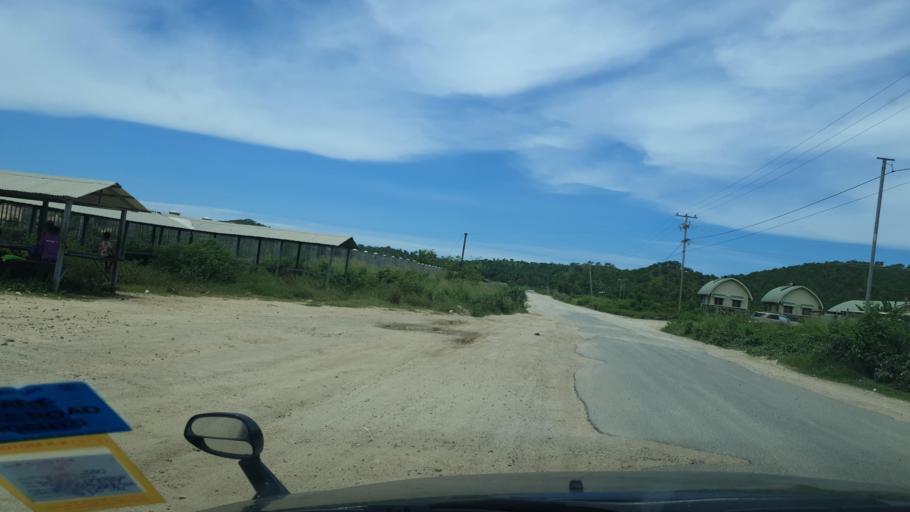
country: PG
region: National Capital
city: Port Moresby
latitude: -9.4198
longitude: 147.0776
